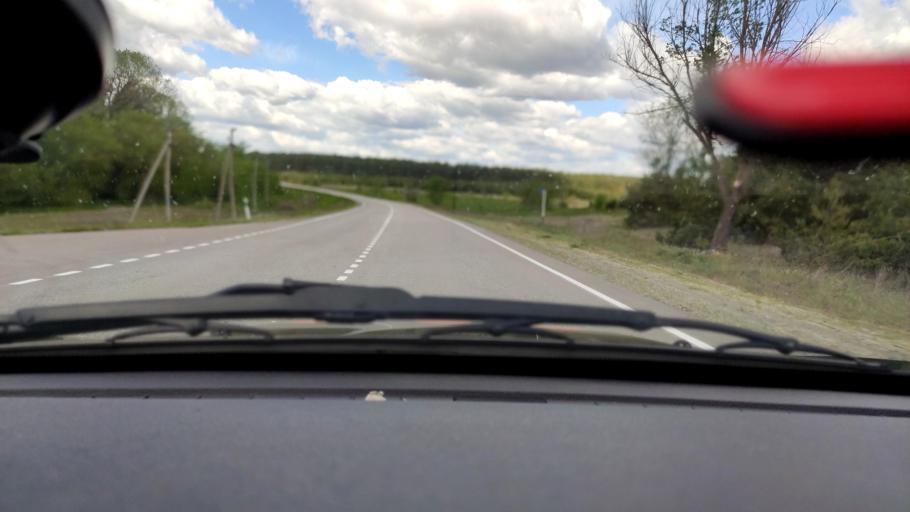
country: RU
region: Voronezj
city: Uryv-Pokrovka
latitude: 51.0545
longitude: 38.9574
